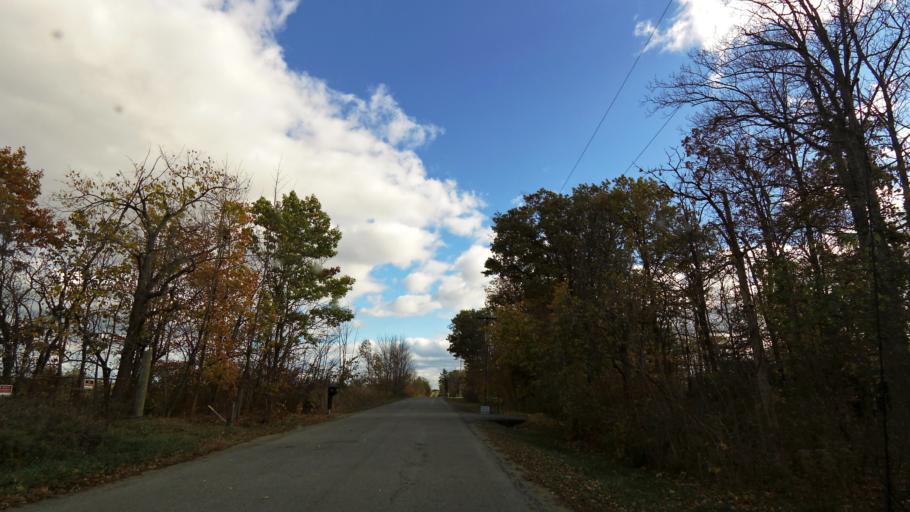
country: CA
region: Ontario
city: Burlington
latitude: 43.4477
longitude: -79.8533
